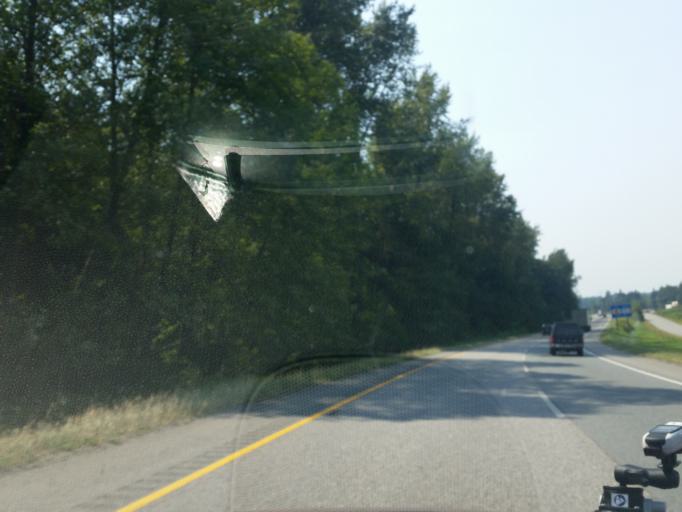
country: CA
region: British Columbia
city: Agassiz
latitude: 49.2072
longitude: -121.7109
